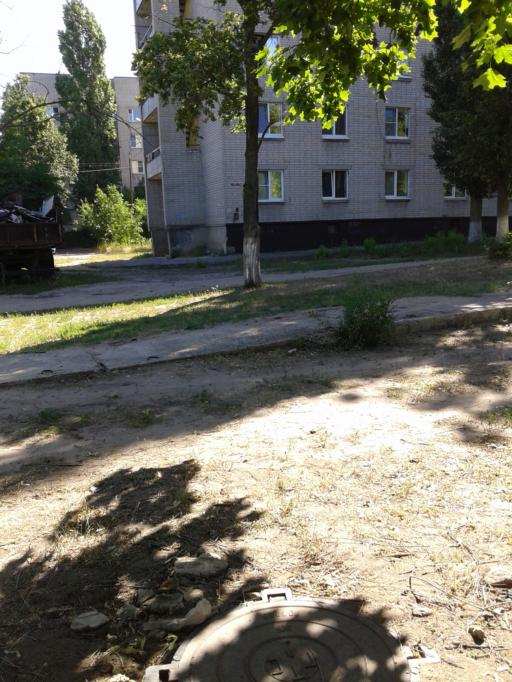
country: RU
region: Voronezj
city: Pridonskoy
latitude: 51.6612
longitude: 39.1249
